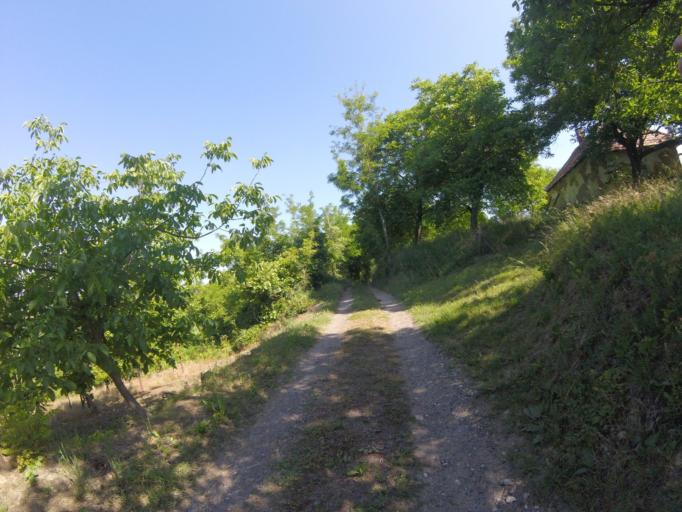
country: HU
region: Zala
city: Zalaszentgrot
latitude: 46.8954
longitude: 17.0682
